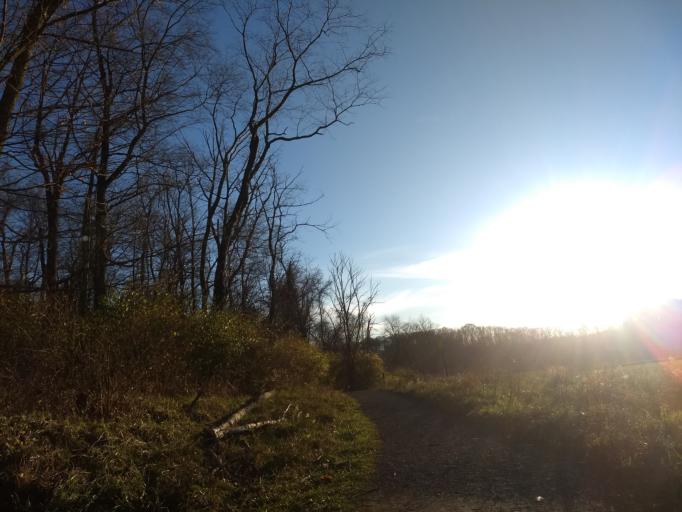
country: US
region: Pennsylvania
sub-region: Allegheny County
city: South Park Township
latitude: 40.3017
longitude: -80.0016
